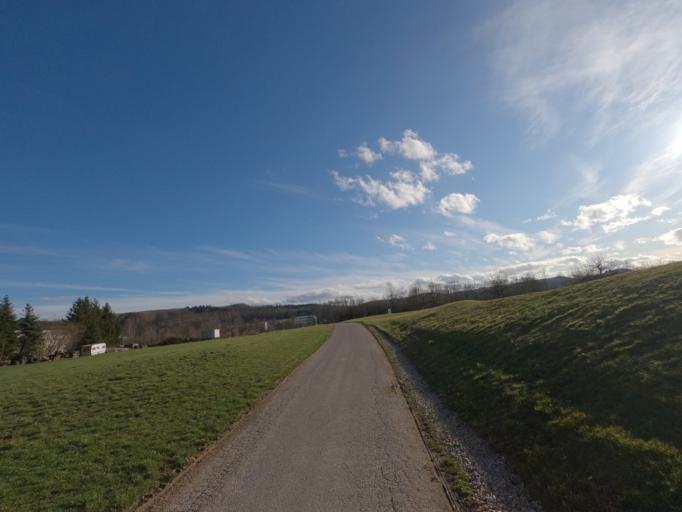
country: DE
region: Baden-Wuerttemberg
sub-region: Regierungsbezirk Stuttgart
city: Donzdorf
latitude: 48.6900
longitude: 9.7921
